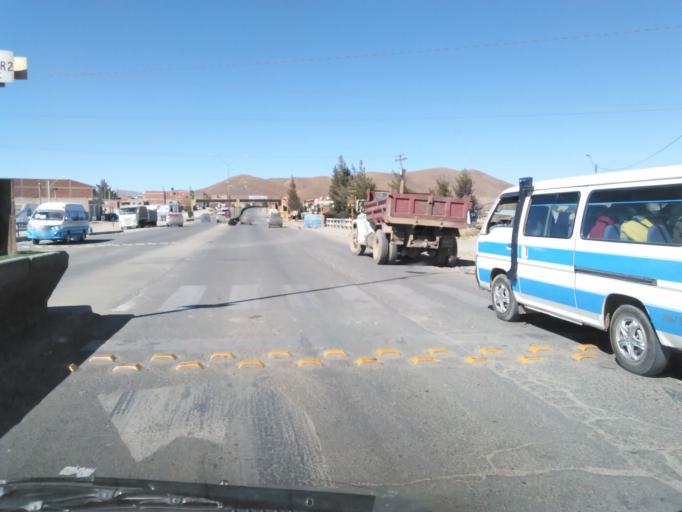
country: BO
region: Oruro
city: Oruro
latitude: -17.9783
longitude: -67.0562
